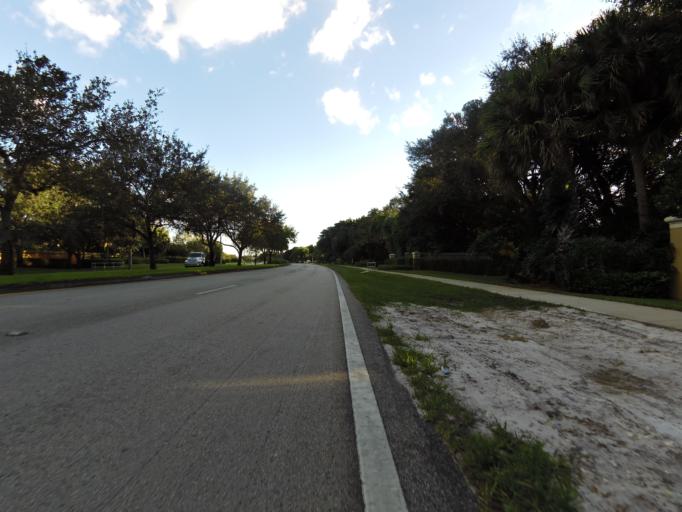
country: US
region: Florida
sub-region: Broward County
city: Pine Island Ridge
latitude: 26.0912
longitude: -80.2840
